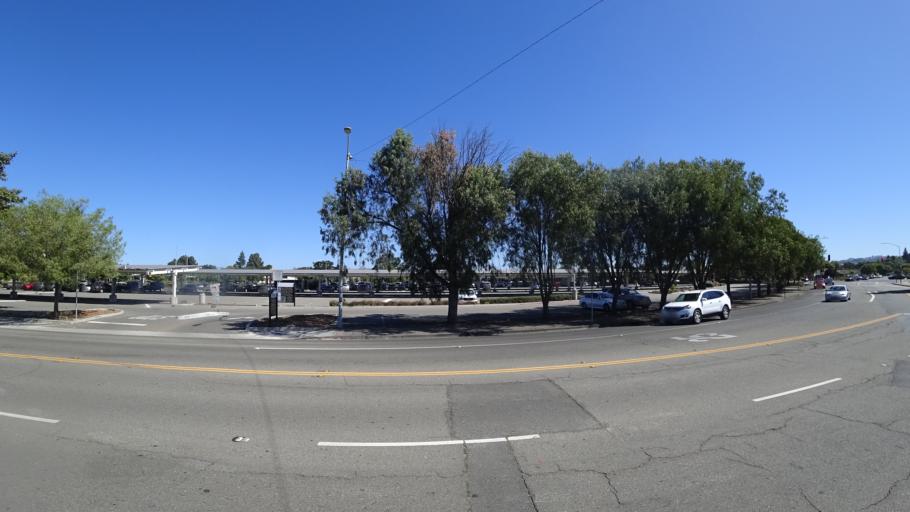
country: US
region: California
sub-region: Alameda County
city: Hayward
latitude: 37.6388
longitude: -122.1034
